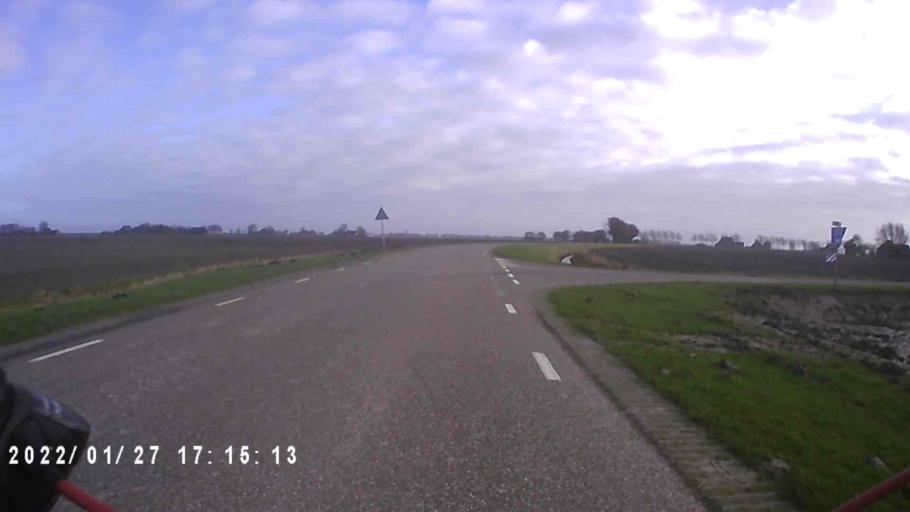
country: NL
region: Friesland
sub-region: Gemeente Dongeradeel
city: Anjum
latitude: 53.3941
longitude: 6.0972
